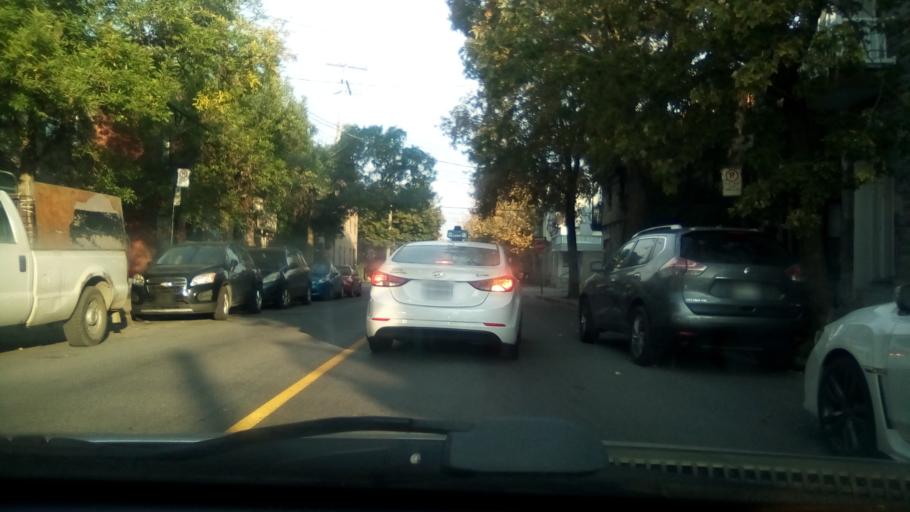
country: CA
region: Quebec
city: Westmount
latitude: 45.4752
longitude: -73.5635
